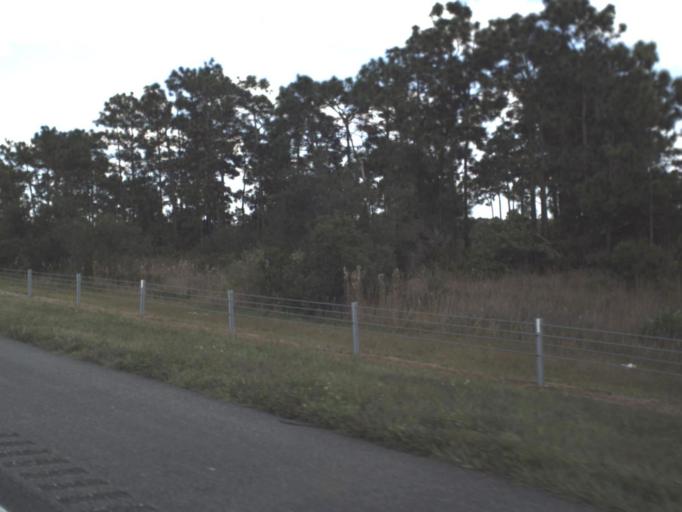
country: US
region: Florida
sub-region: Indian River County
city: Fellsmere
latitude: 27.8154
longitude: -81.0022
